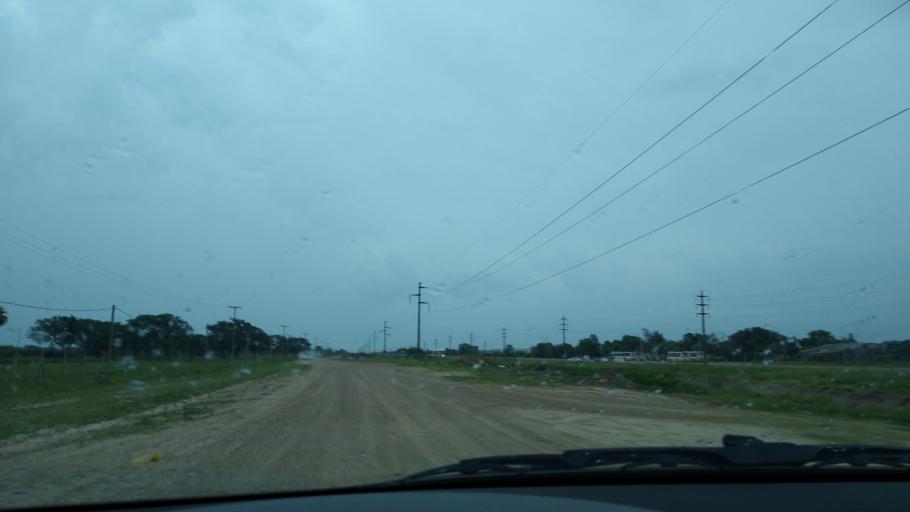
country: AR
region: Chaco
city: Puerto Vilelas
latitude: -27.4996
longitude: -58.9762
